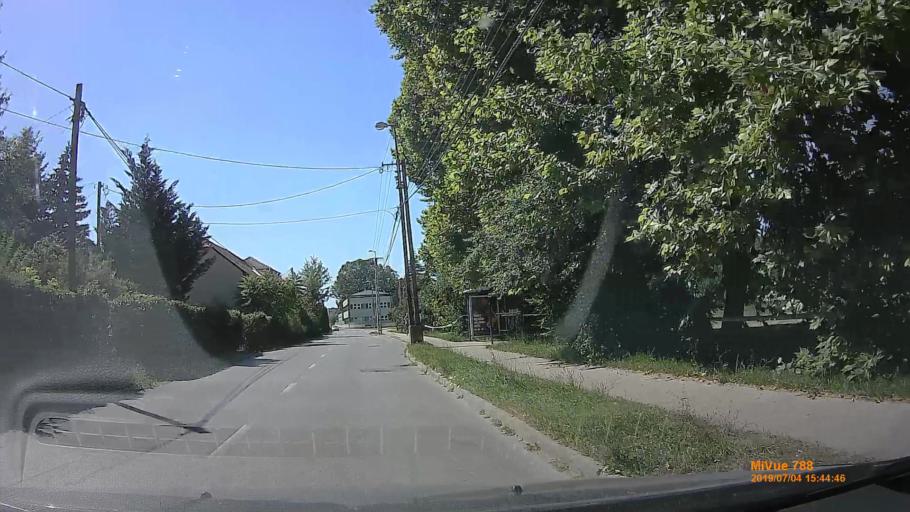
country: HU
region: Komarom-Esztergom
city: Tatabanya
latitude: 47.5685
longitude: 18.4156
